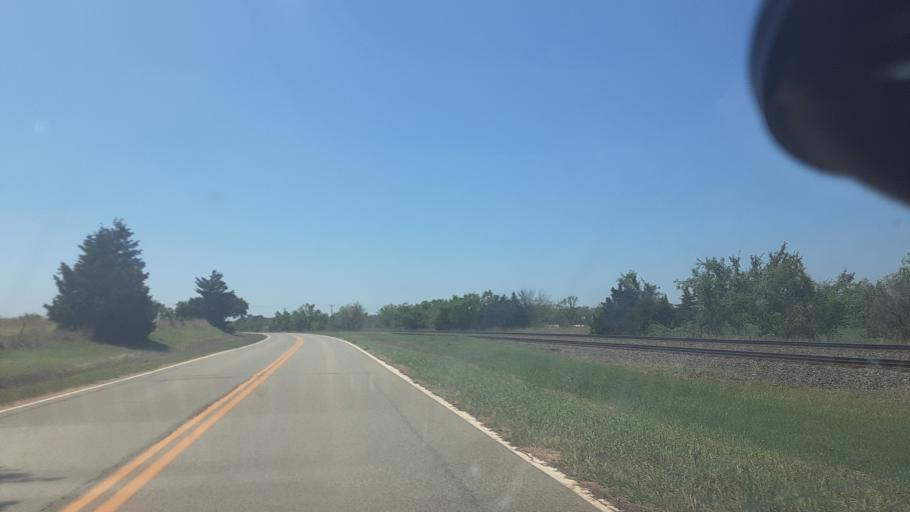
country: US
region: Oklahoma
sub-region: Logan County
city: Guthrie
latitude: 36.0748
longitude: -97.4042
